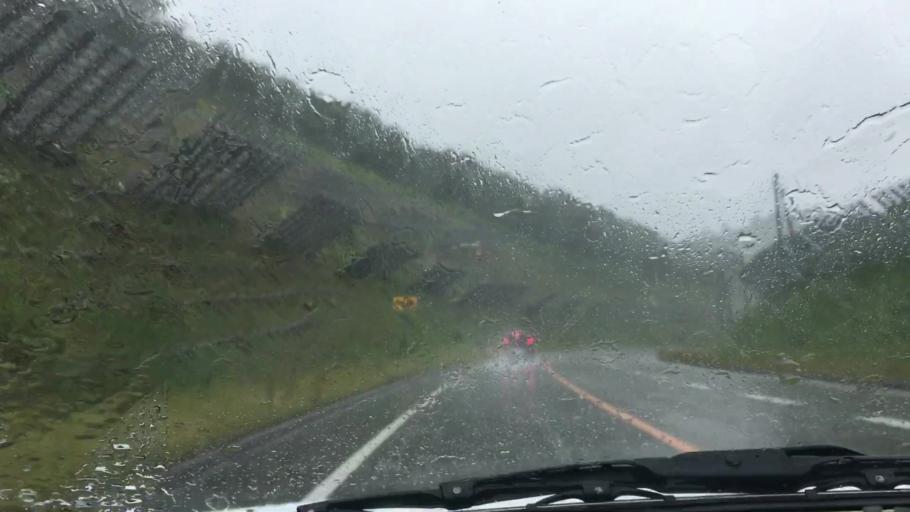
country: JP
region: Hokkaido
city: Sapporo
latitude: 42.8476
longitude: 141.0829
